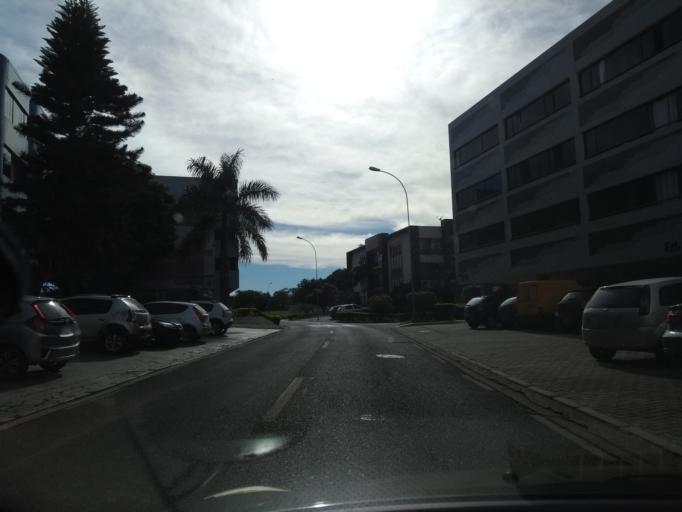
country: BR
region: Federal District
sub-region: Brasilia
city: Brasilia
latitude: -15.7928
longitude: -47.9301
